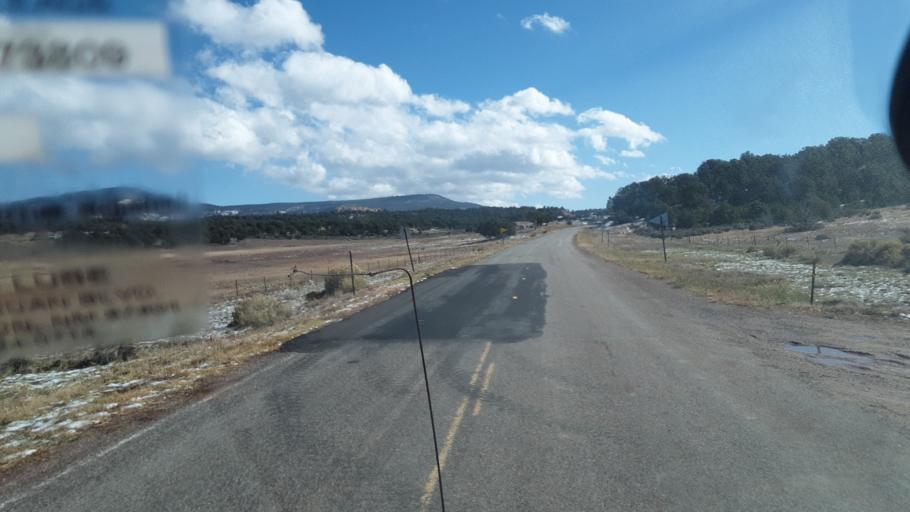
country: US
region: New Mexico
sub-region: Rio Arriba County
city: Santa Teresa
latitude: 36.2352
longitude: -106.8438
